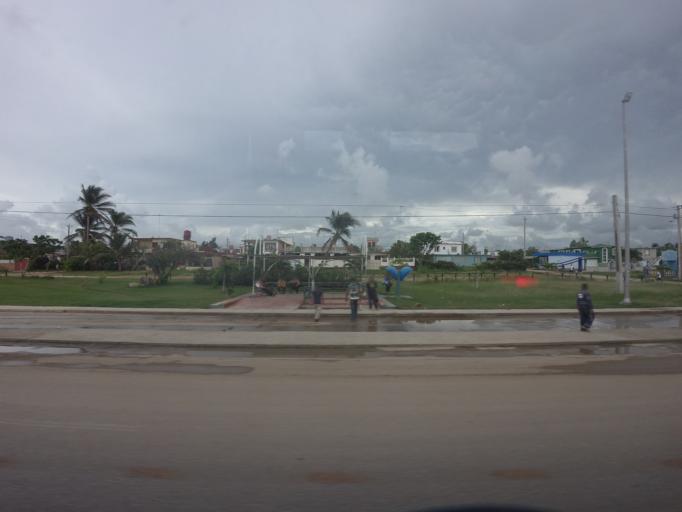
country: CU
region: Matanzas
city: Varadero
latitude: 23.1125
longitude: -81.3628
